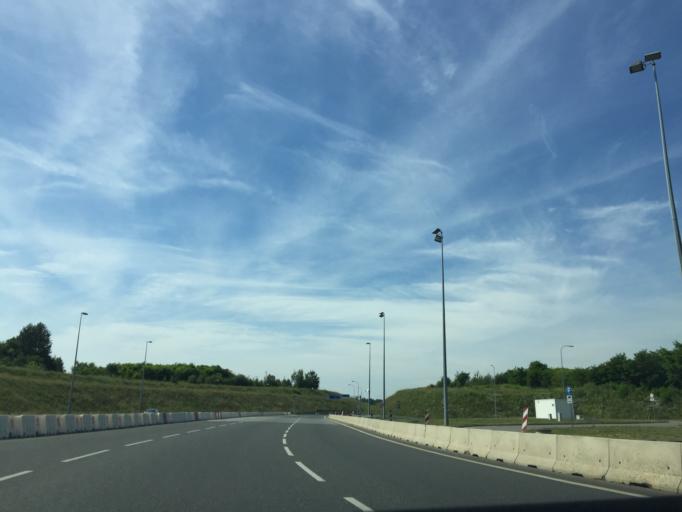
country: PL
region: Silesian Voivodeship
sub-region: Piekary Slaskie
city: Piekary Slaskie
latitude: 50.3656
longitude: 18.9360
